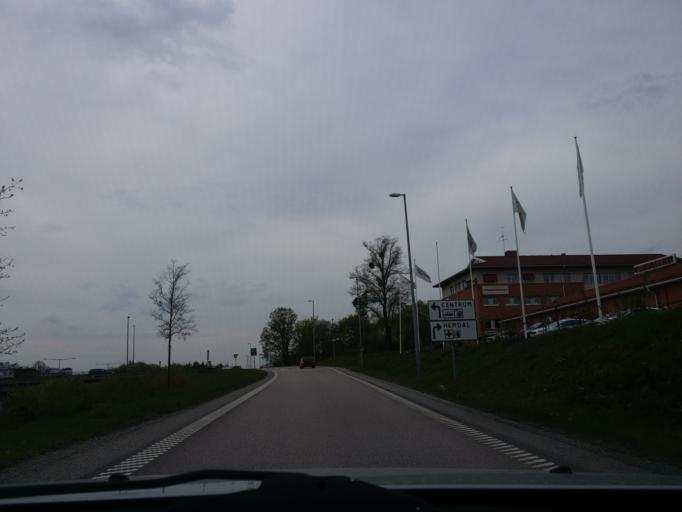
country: SE
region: Vaestmanland
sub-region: Vasteras
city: Vasteras
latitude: 59.6134
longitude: 16.5751
